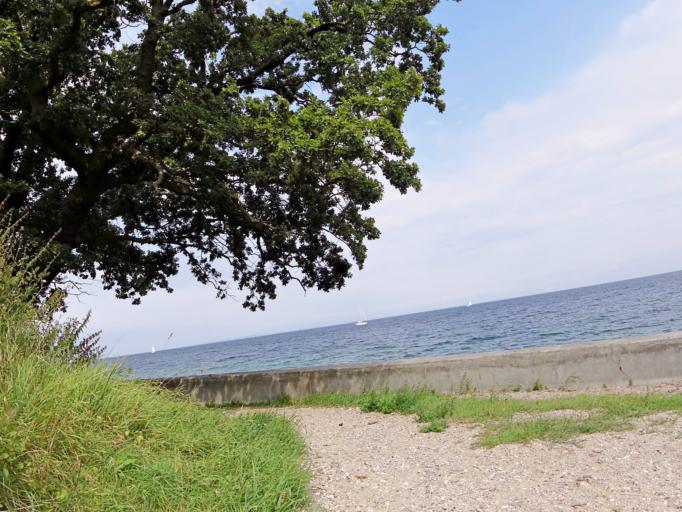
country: DK
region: Capital Region
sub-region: Gentofte Kommune
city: Charlottenlund
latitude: 55.7961
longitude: 12.5899
